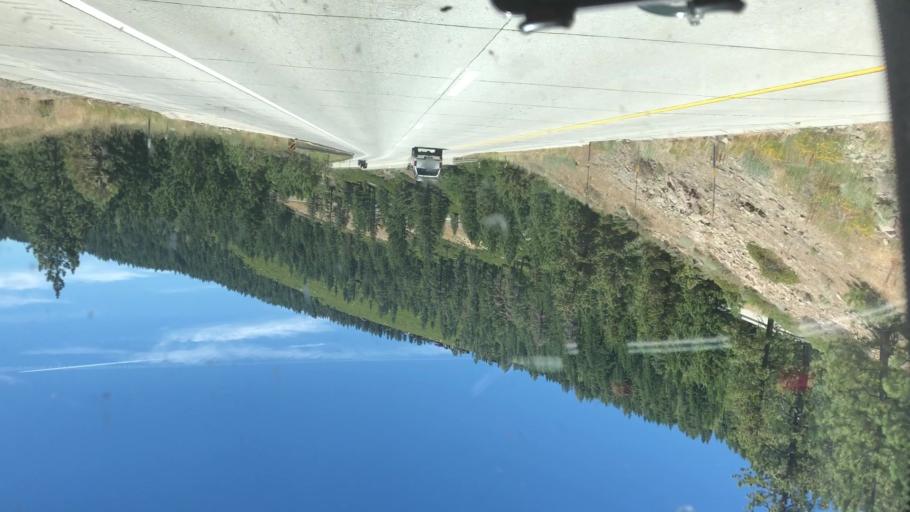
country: US
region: California
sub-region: Nevada County
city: Truckee
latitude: 39.3300
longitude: -120.2621
